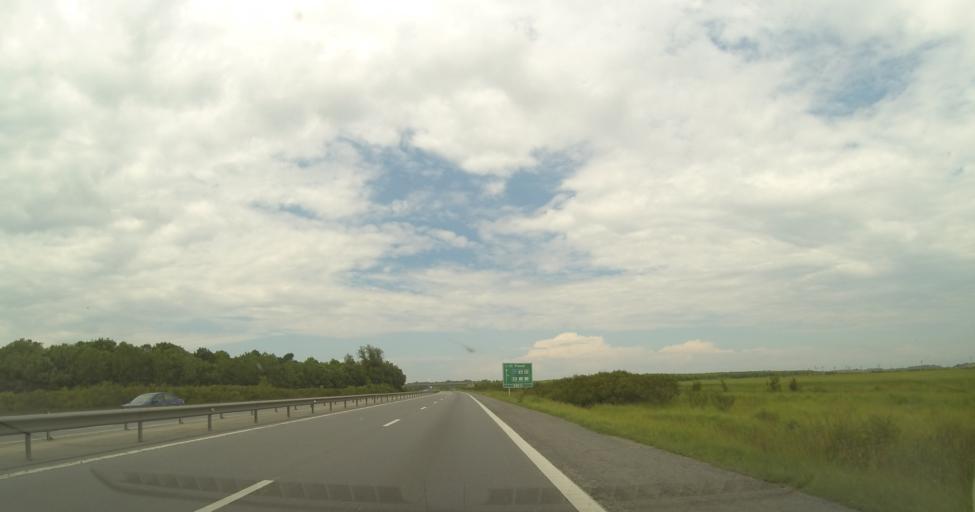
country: RO
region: Dambovita
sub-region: Comuna Corbii Mari
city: Grozavesti
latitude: 44.5992
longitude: 25.4587
